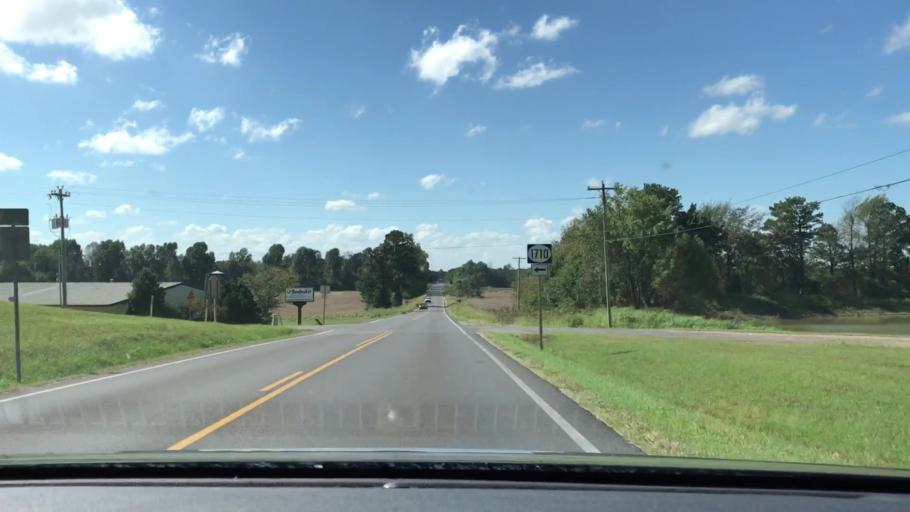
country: US
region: Kentucky
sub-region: Graves County
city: Mayfield
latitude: 36.7531
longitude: -88.6106
